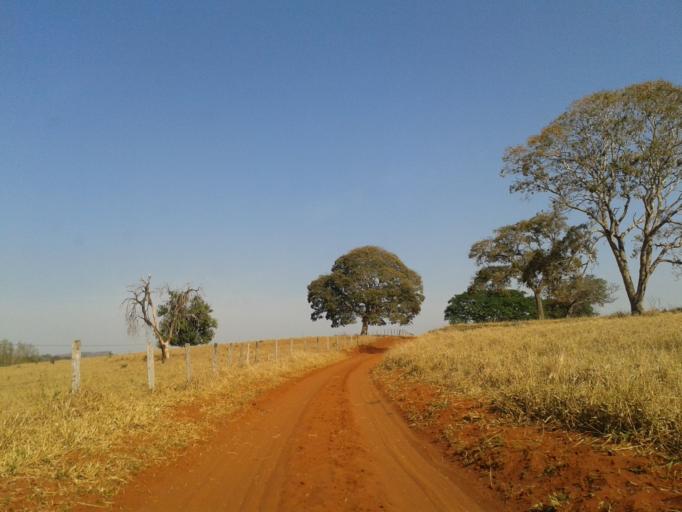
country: BR
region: Minas Gerais
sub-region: Santa Vitoria
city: Santa Vitoria
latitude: -19.1627
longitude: -50.0142
